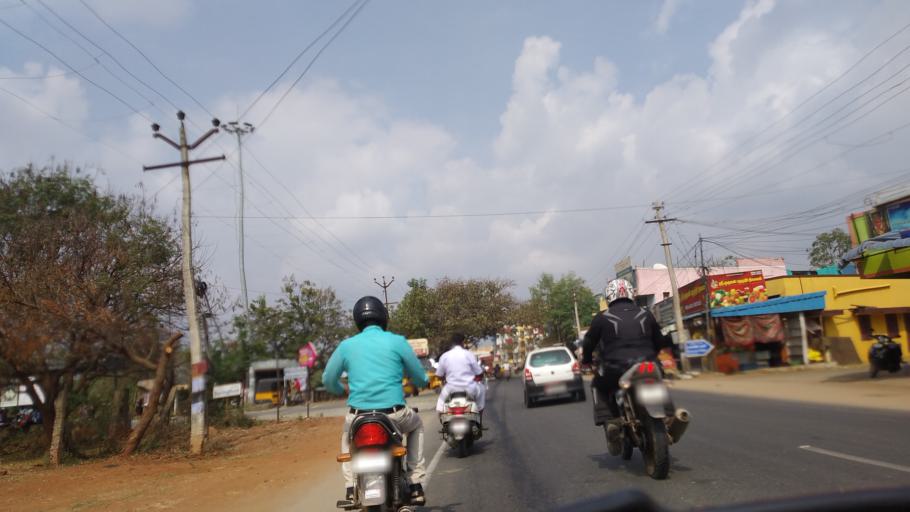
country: IN
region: Tamil Nadu
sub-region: Coimbatore
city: Perur
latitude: 10.9439
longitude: 76.9400
